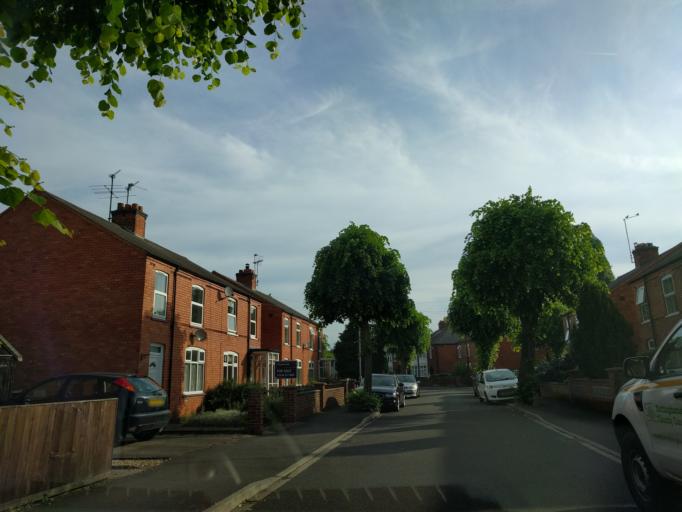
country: GB
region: England
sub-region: Nottinghamshire
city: Newark on Trent
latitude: 53.0704
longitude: -0.8120
